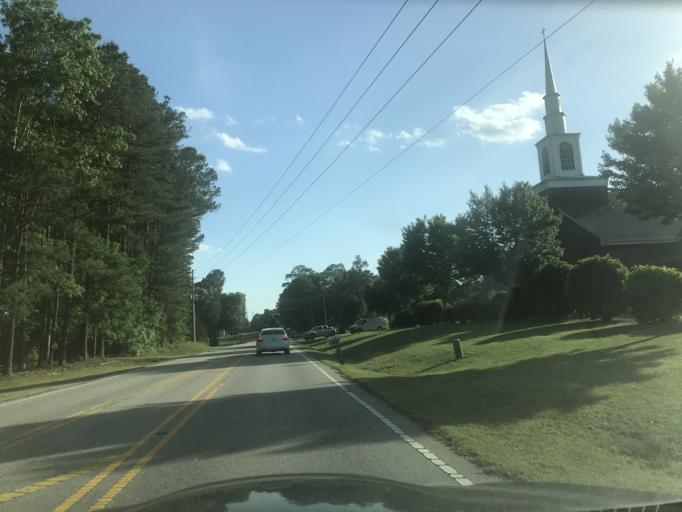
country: US
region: North Carolina
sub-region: Wake County
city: Wendell
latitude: 35.7677
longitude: -78.4084
